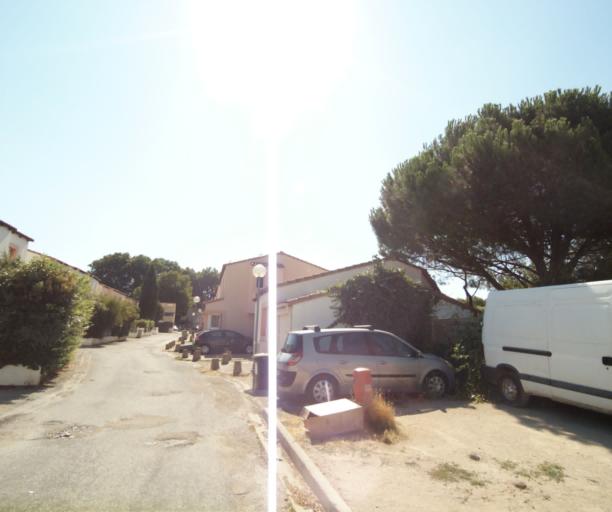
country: FR
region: Languedoc-Roussillon
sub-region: Departement de l'Herault
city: Marsillargues
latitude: 43.6695
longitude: 4.1733
